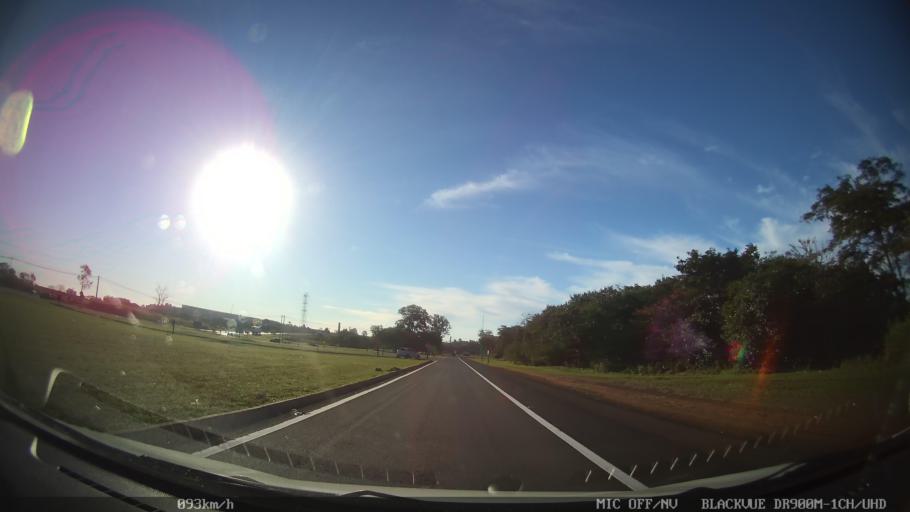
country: BR
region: Sao Paulo
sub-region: Americo Brasiliense
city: Americo Brasiliense
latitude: -21.7576
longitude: -48.1190
